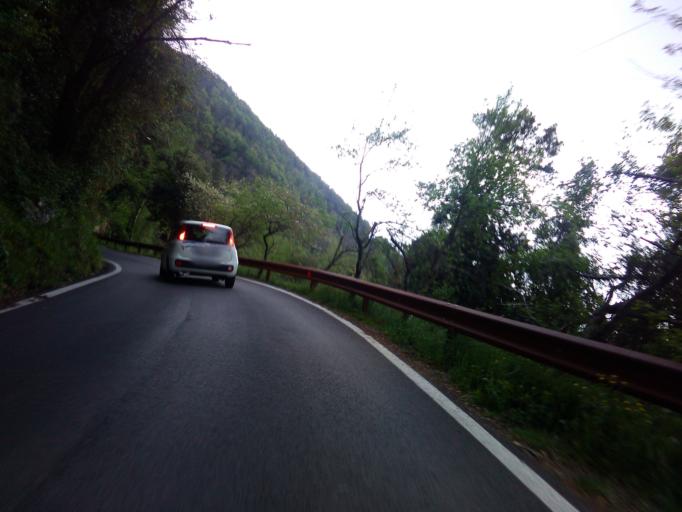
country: IT
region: Tuscany
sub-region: Provincia di Lucca
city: Pontestazzemese
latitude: 43.9643
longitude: 10.2791
